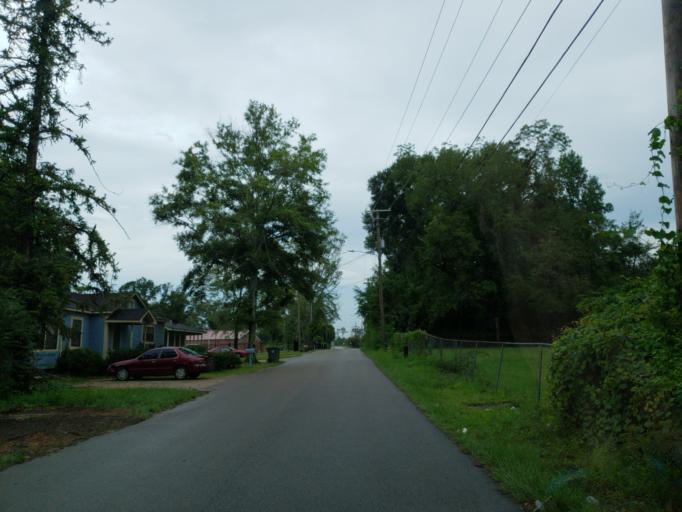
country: US
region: Mississippi
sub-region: Forrest County
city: Hattiesburg
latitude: 31.3030
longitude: -89.2867
